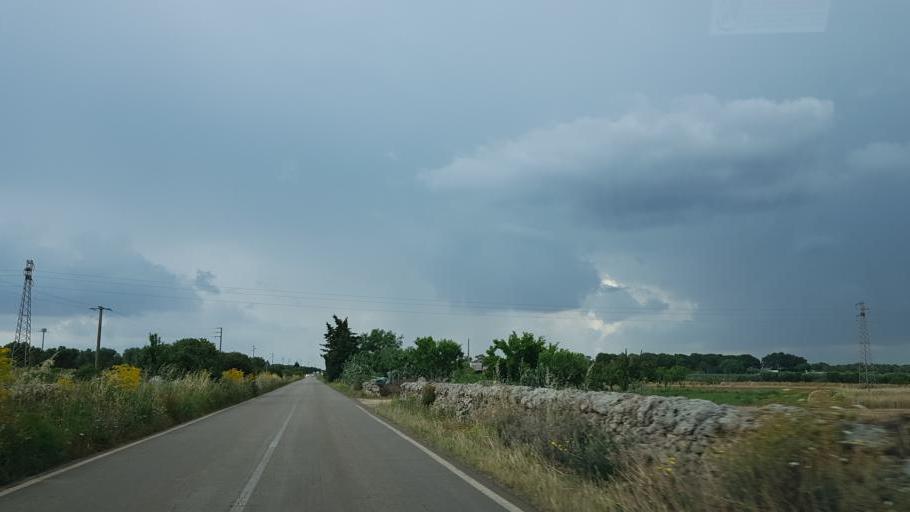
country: IT
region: Apulia
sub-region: Provincia di Lecce
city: Porto Cesareo
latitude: 40.3210
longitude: 17.8575
